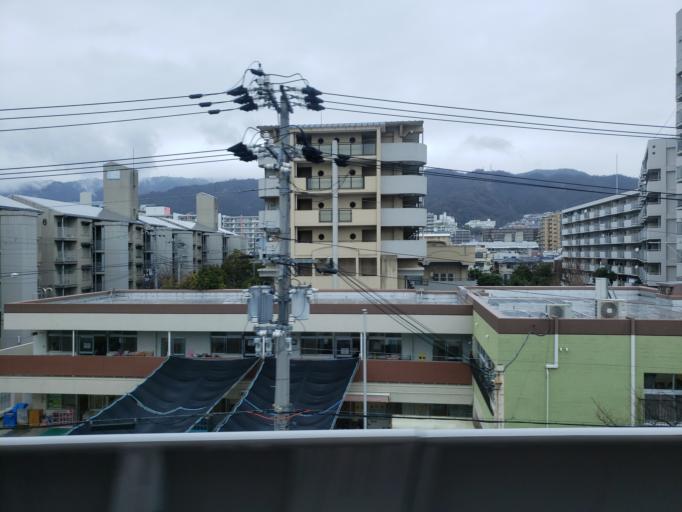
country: JP
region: Hyogo
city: Ashiya
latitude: 34.7208
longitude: 135.2869
